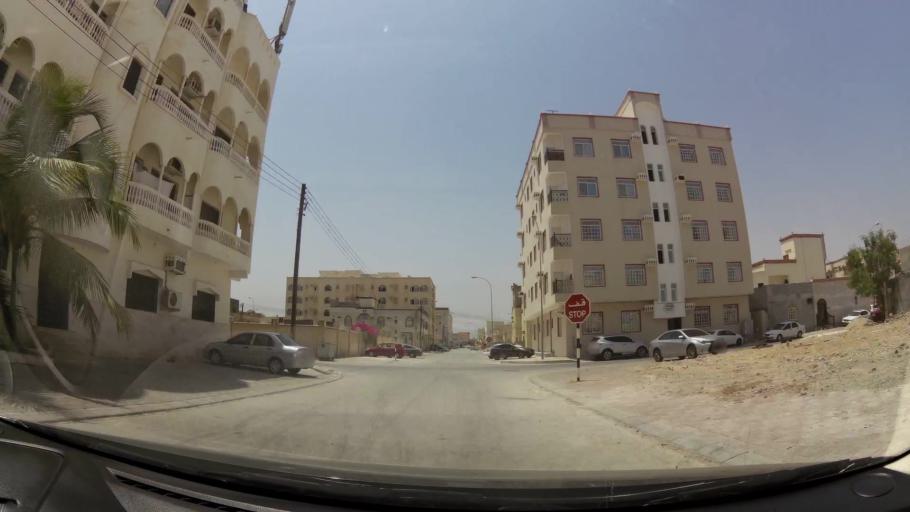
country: OM
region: Zufar
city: Salalah
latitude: 17.0181
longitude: 54.0793
